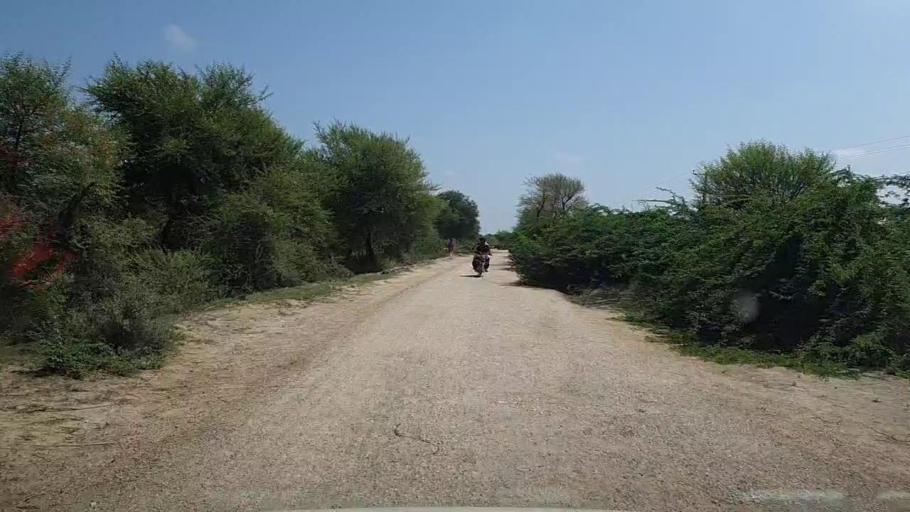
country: PK
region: Sindh
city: Kario
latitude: 24.8499
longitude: 68.6920
